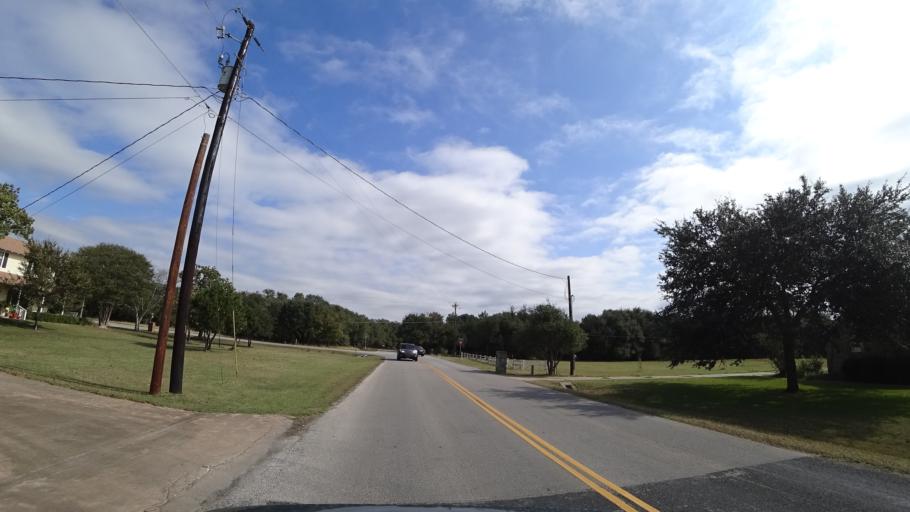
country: US
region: Texas
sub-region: Williamson County
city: Brushy Creek
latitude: 30.5240
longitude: -97.7364
